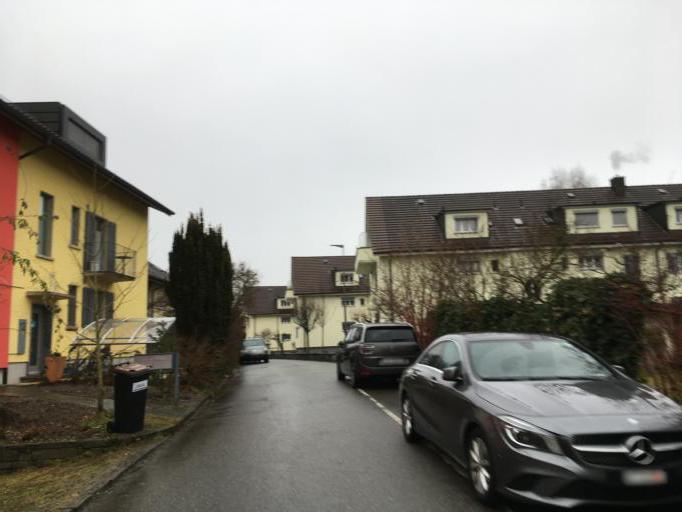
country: CH
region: Bern
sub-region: Bern-Mittelland District
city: Bolligen
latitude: 46.9579
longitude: 7.4781
